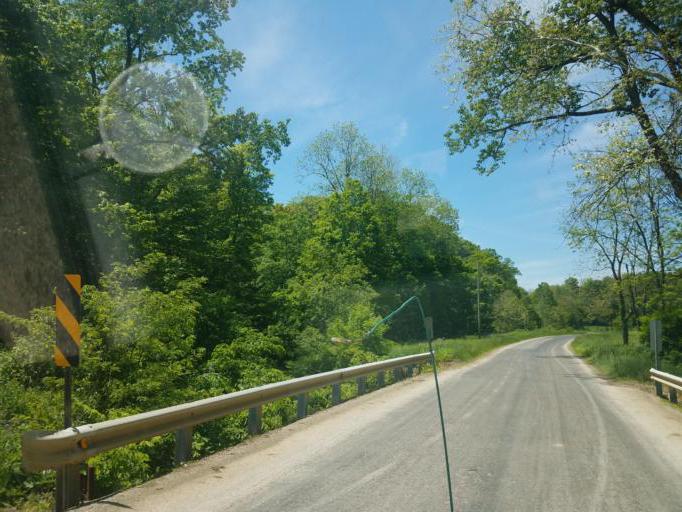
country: US
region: Ohio
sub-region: Huron County
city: New London
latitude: 40.9675
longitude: -82.3980
